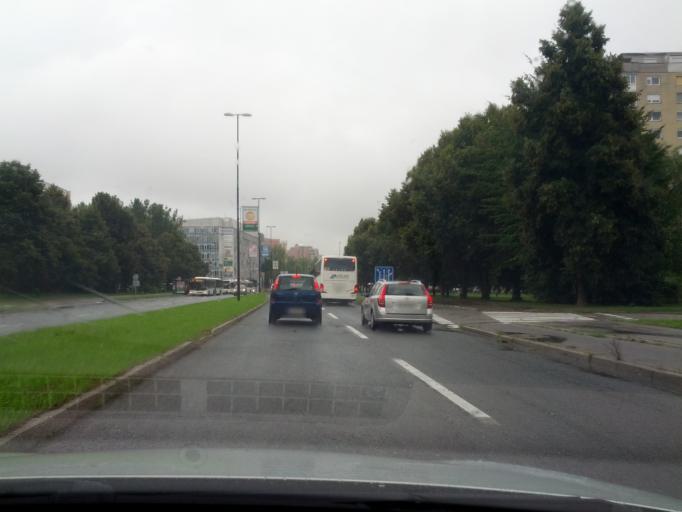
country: SI
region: Ljubljana
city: Ljubljana
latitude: 46.0751
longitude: 14.4842
